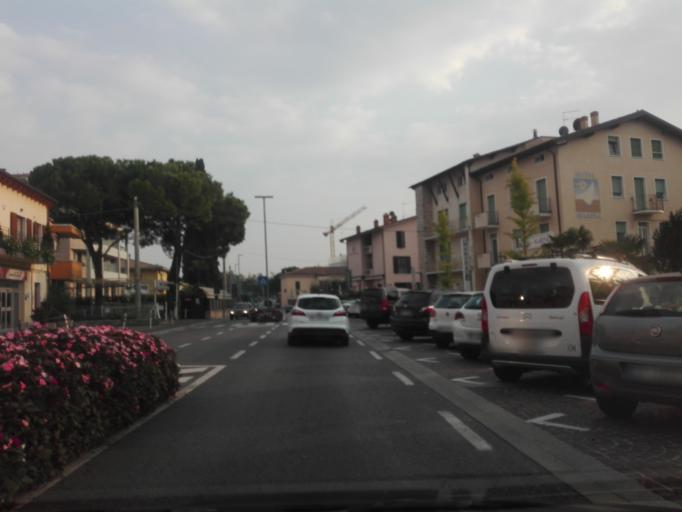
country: IT
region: Veneto
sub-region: Provincia di Verona
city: Bardolino
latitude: 45.5490
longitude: 10.7232
